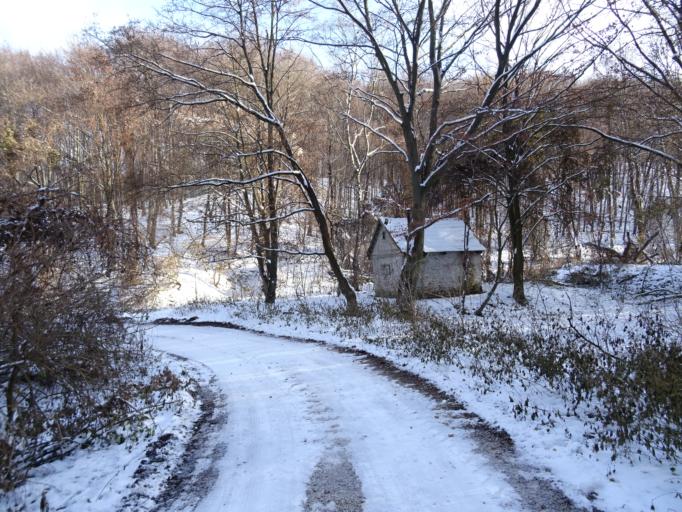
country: HU
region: Fejer
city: Pusztavam
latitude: 47.3923
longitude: 18.2614
